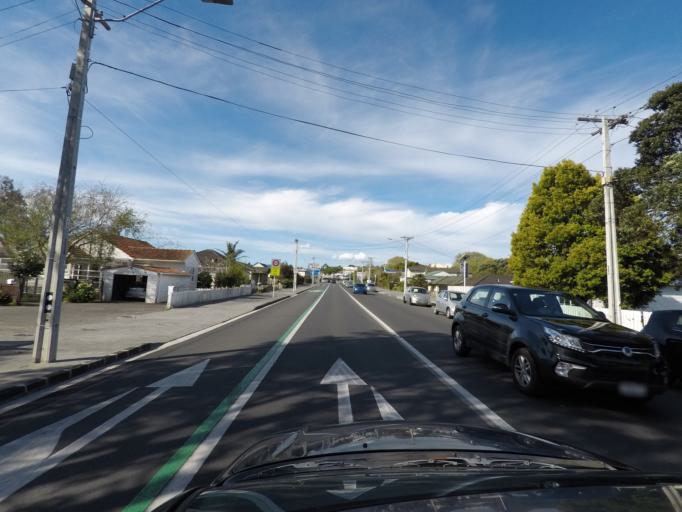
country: NZ
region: Auckland
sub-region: Auckland
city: Rosebank
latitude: -36.9002
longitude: 174.6949
